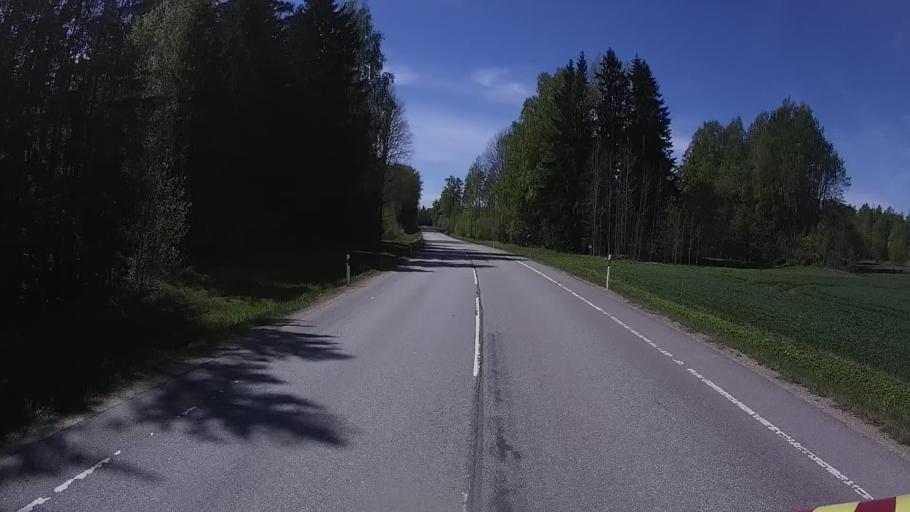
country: EE
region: Vorumaa
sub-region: Voru linn
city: Voru
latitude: 57.8862
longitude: 27.1506
